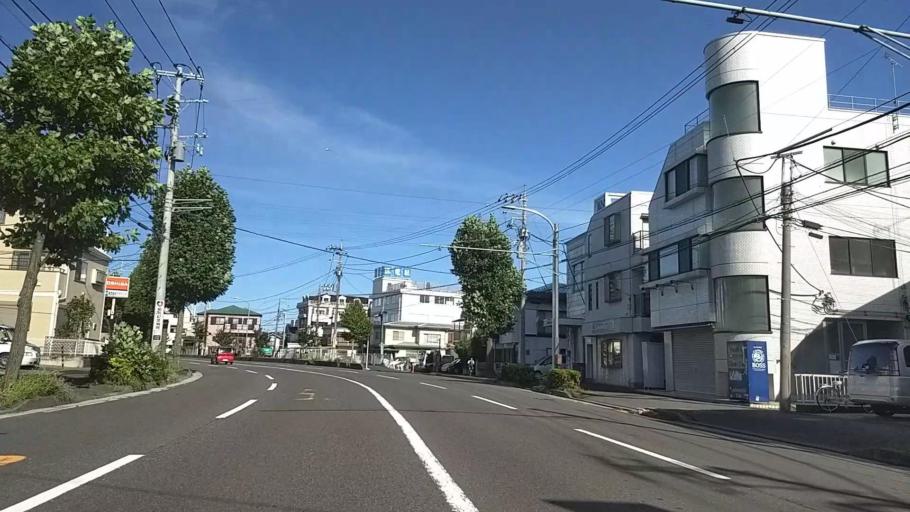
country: JP
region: Kanagawa
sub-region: Kawasaki-shi
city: Kawasaki
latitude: 35.5340
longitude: 139.6639
